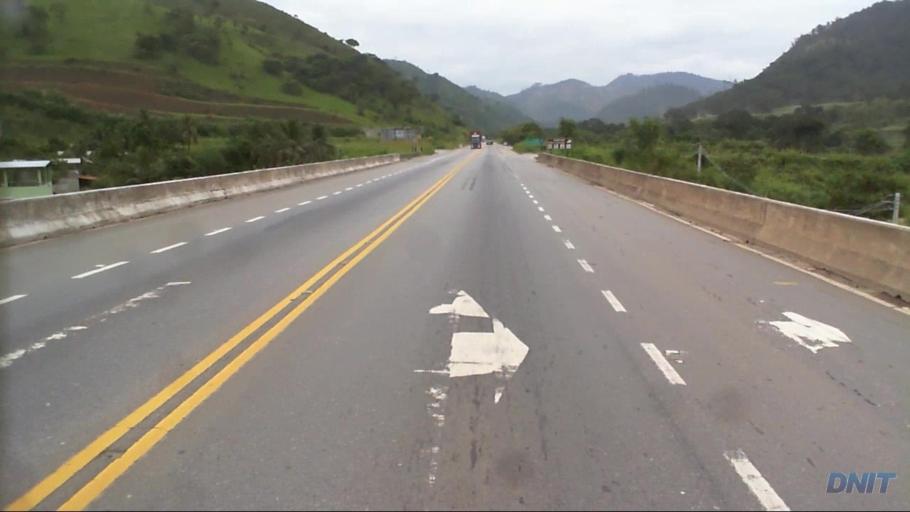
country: BR
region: Minas Gerais
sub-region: Timoteo
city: Timoteo
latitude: -19.5395
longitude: -42.6850
